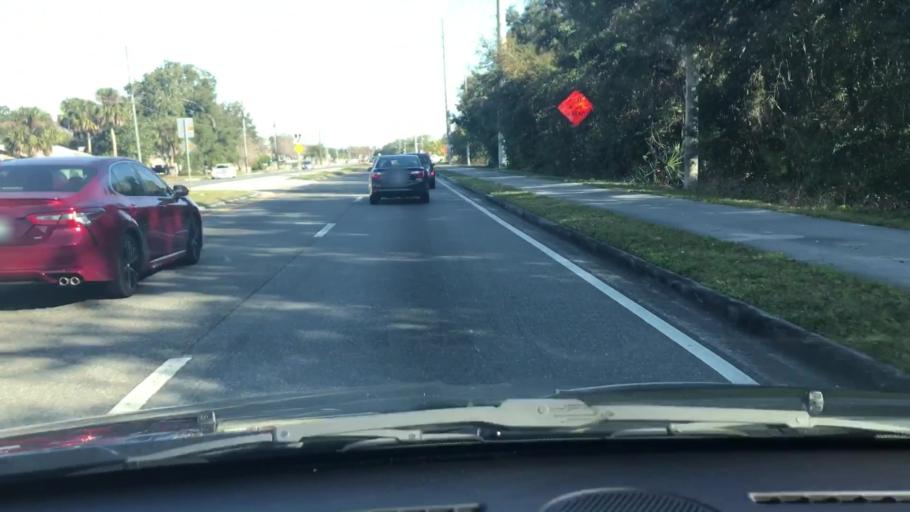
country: US
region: Florida
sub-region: Osceola County
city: Campbell
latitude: 28.2562
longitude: -81.4363
